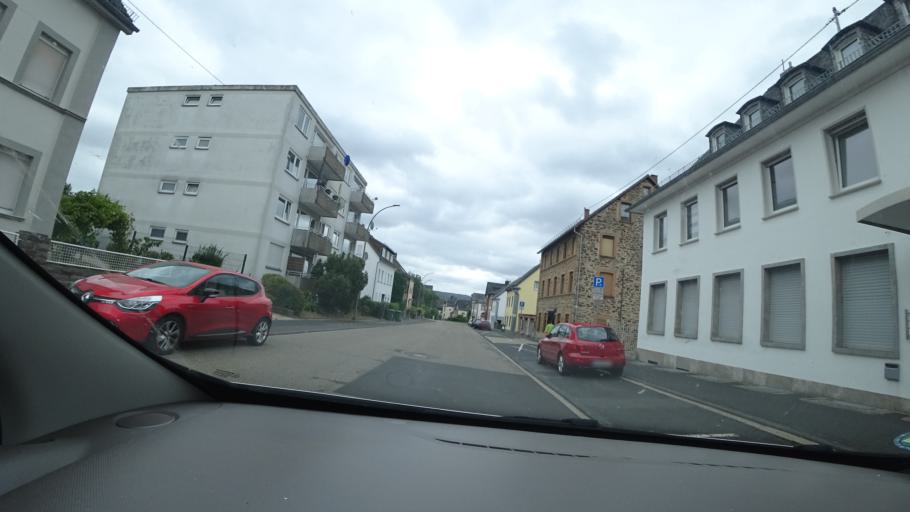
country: DE
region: Rheinland-Pfalz
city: Hohr-Grenzhausen
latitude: 50.4374
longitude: 7.6601
